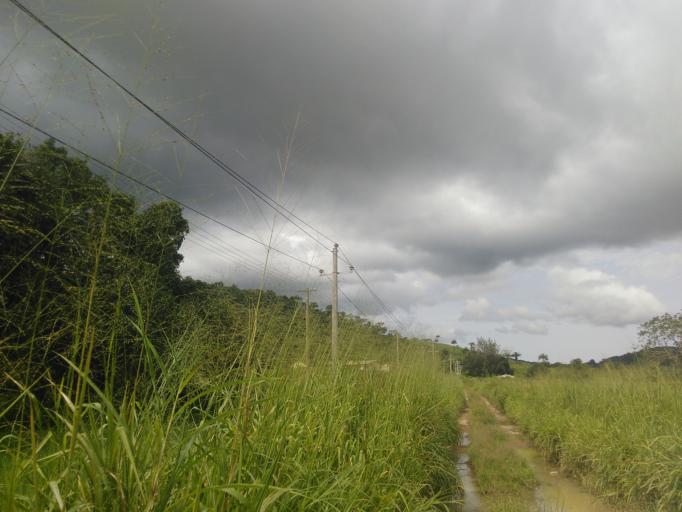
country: SL
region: Northern Province
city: Makali
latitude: 8.6292
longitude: -11.6601
